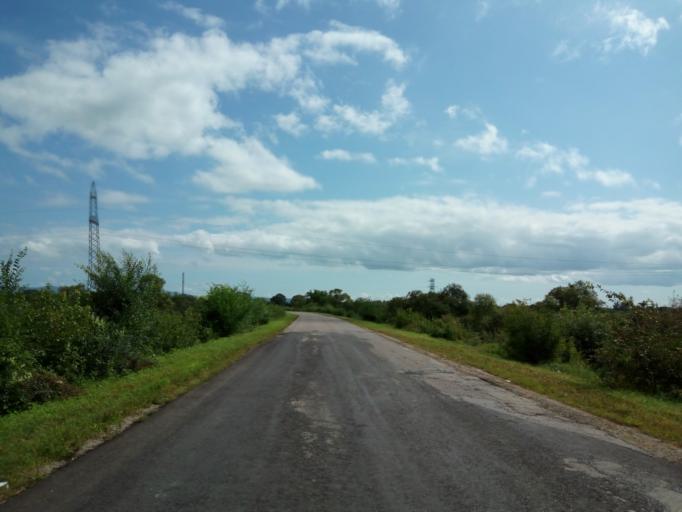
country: RU
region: Primorskiy
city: Dal'nerechensk
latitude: 45.9703
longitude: 133.7813
